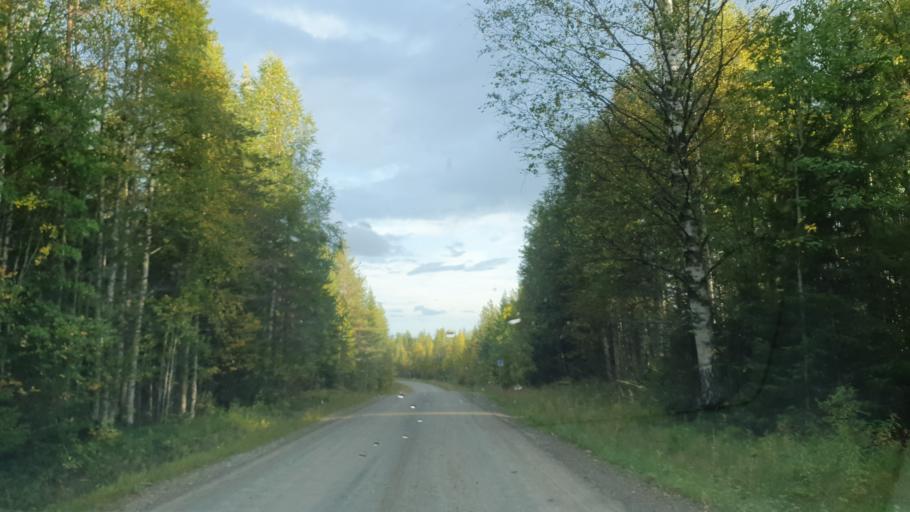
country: FI
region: Kainuu
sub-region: Kehys-Kainuu
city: Kuhmo
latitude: 64.4307
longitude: 29.3230
